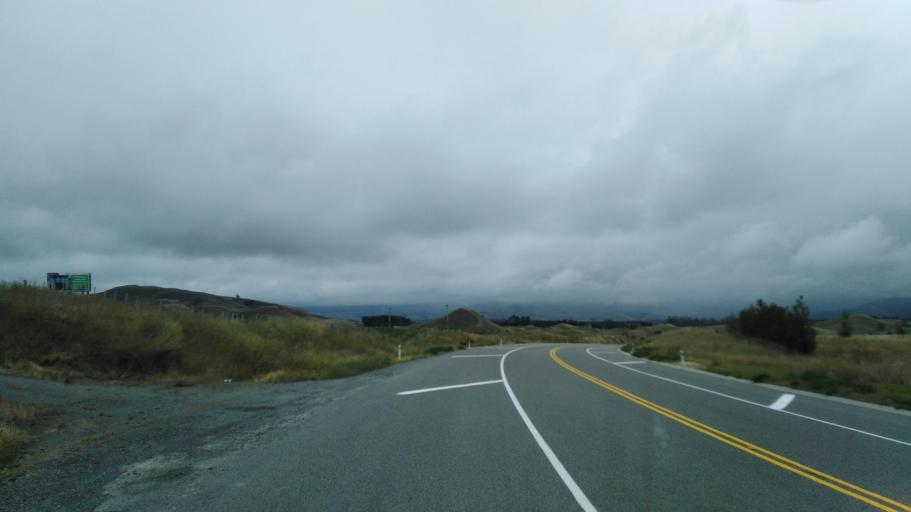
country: NZ
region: Marlborough
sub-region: Marlborough District
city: Blenheim
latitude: -41.6922
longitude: 174.0811
